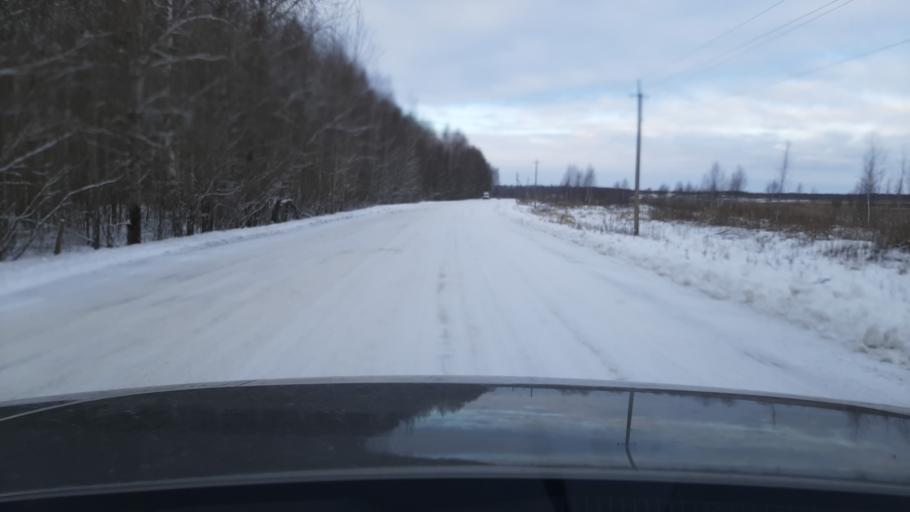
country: RU
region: Kostroma
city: Nerekhta
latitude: 57.4708
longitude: 40.6769
